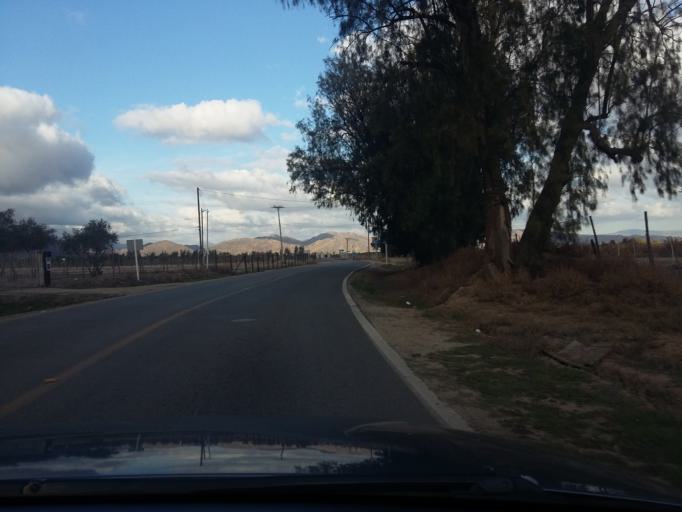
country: MX
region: Baja California
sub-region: Ensenada
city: Rancho Verde
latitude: 32.0588
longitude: -116.6473
